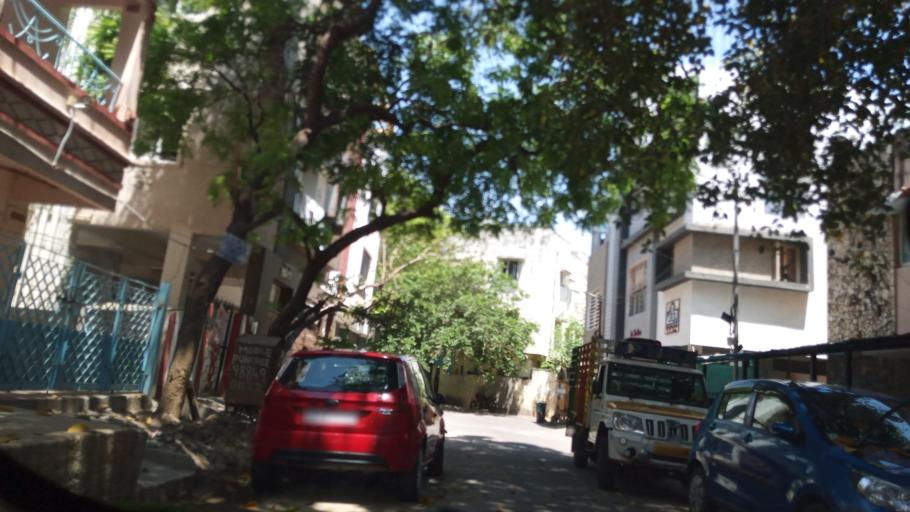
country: IN
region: Tamil Nadu
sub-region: Kancheepuram
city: Alandur
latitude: 13.0367
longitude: 80.2220
